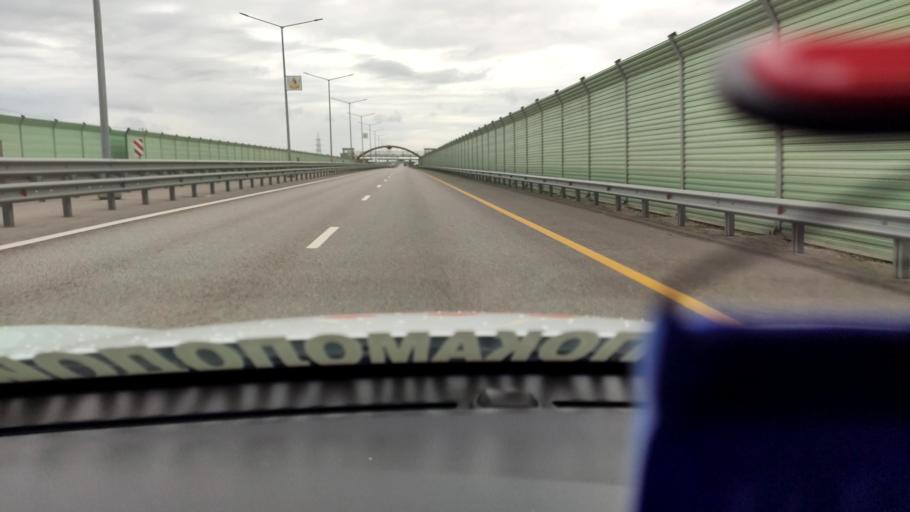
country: RU
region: Voronezj
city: Novaya Usman'
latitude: 51.6252
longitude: 39.3177
